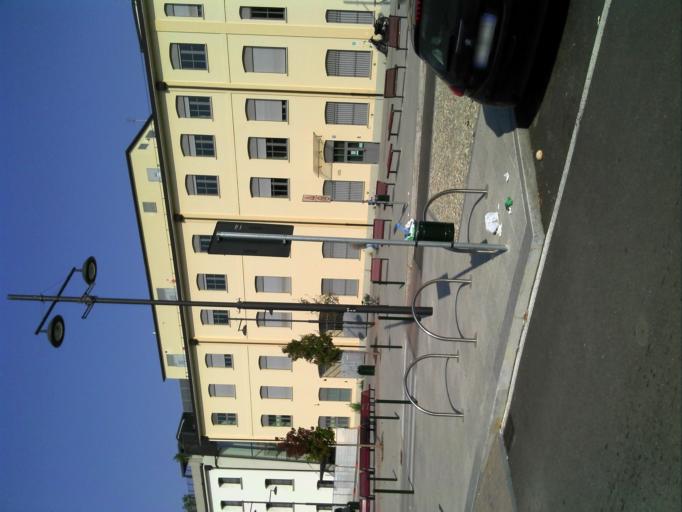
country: IT
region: Piedmont
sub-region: Provincia di Torino
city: Turin
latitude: 45.0899
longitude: 7.6859
